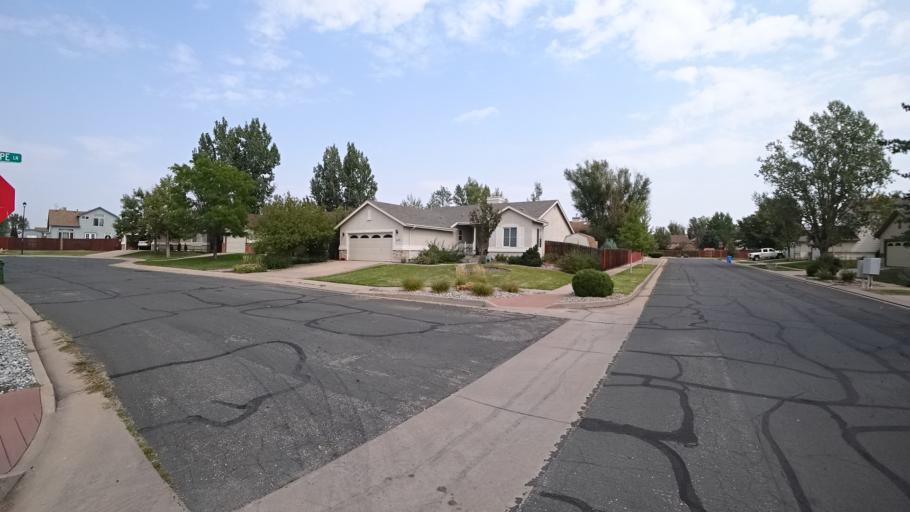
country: US
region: Colorado
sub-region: El Paso County
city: Cimarron Hills
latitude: 38.8212
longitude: -104.7413
